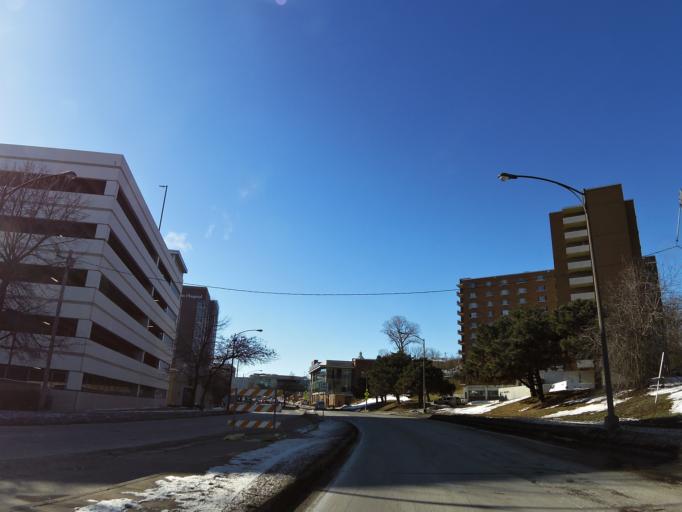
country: US
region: Minnesota
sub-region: Ramsey County
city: Saint Paul
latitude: 44.9579
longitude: -93.0929
